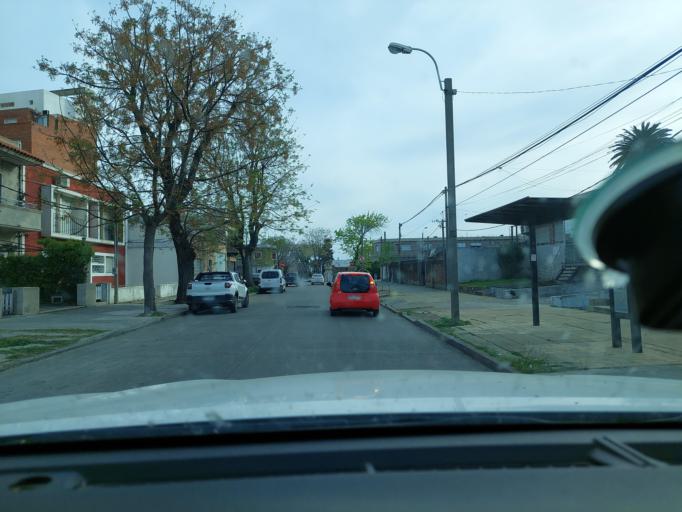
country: UY
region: Montevideo
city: Montevideo
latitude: -34.8735
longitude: -56.1587
